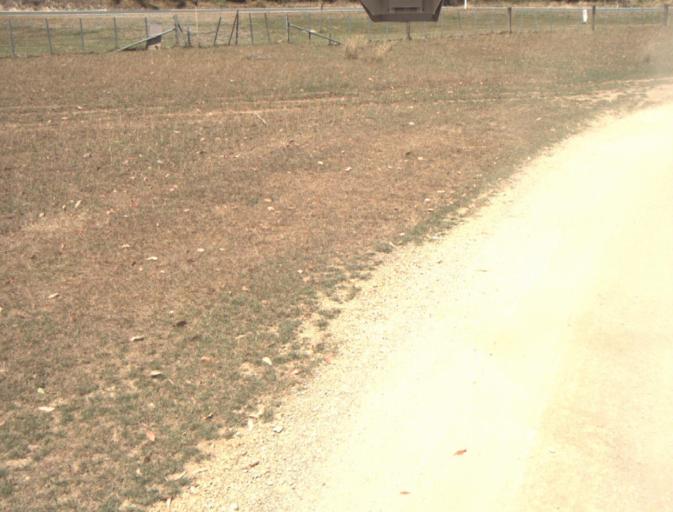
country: AU
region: Tasmania
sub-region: Dorset
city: Scottsdale
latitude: -41.3006
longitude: 147.3818
